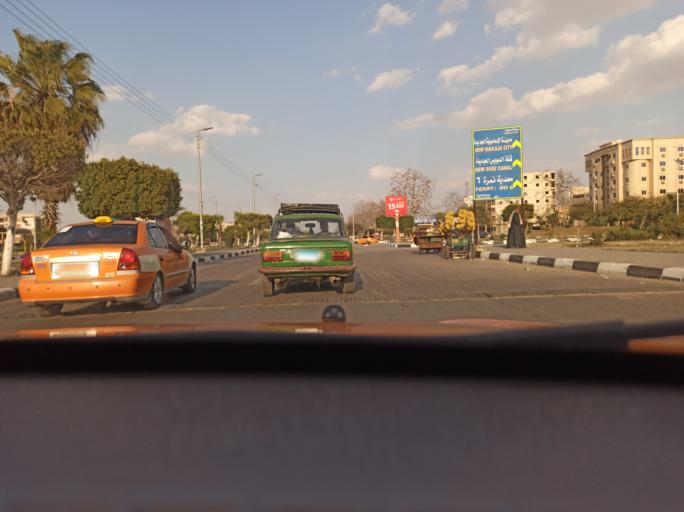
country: EG
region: Al Isma'iliyah
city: Ismailia
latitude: 30.6203
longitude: 32.2814
